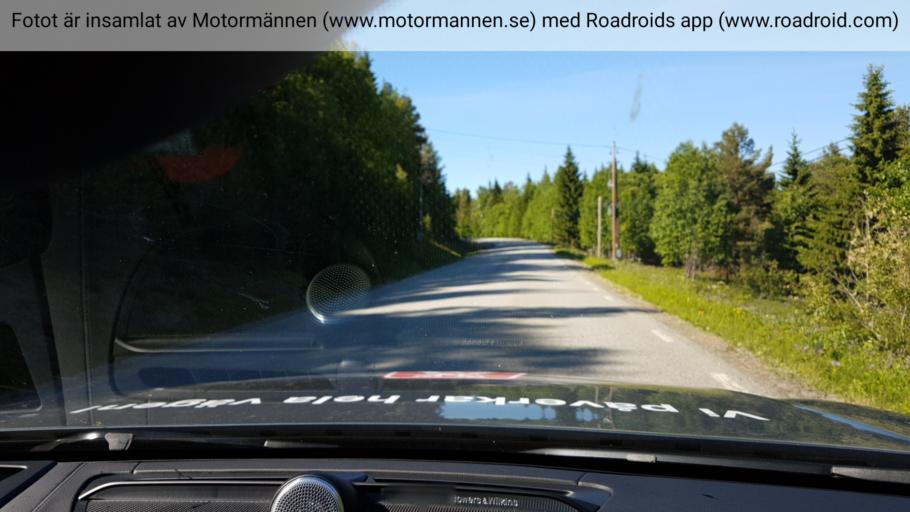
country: SE
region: Jaemtland
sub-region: Bergs Kommun
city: Hoverberg
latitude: 62.7263
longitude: 14.5999
